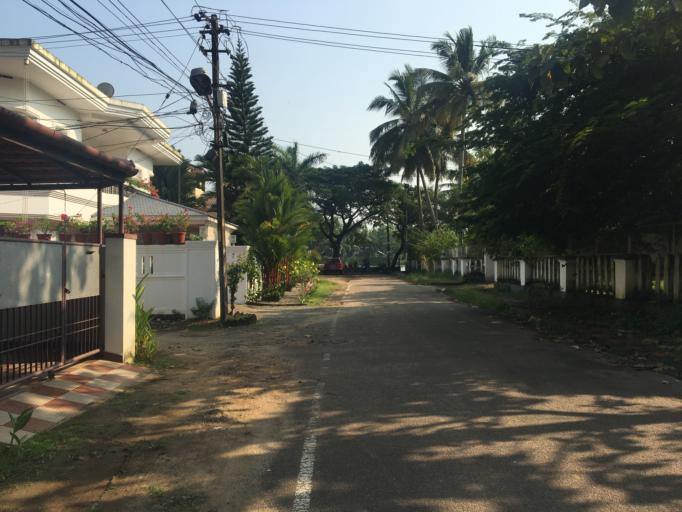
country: IN
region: Kerala
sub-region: Ernakulam
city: Cochin
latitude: 9.9503
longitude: 76.3118
